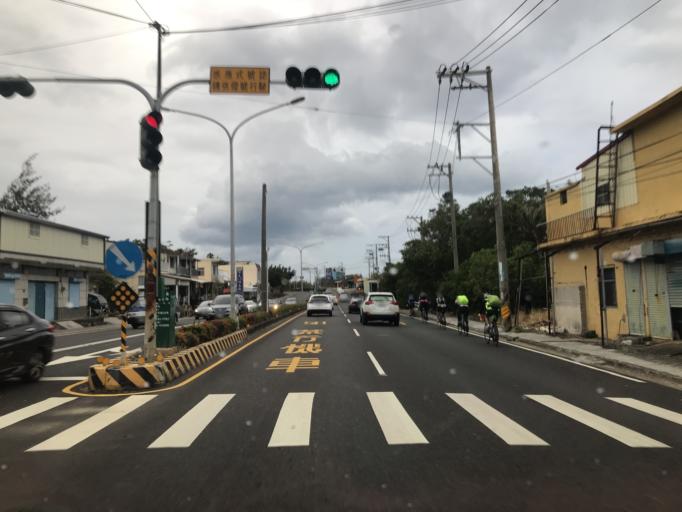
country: TW
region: Taiwan
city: Hengchun
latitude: 22.1892
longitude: 120.6918
